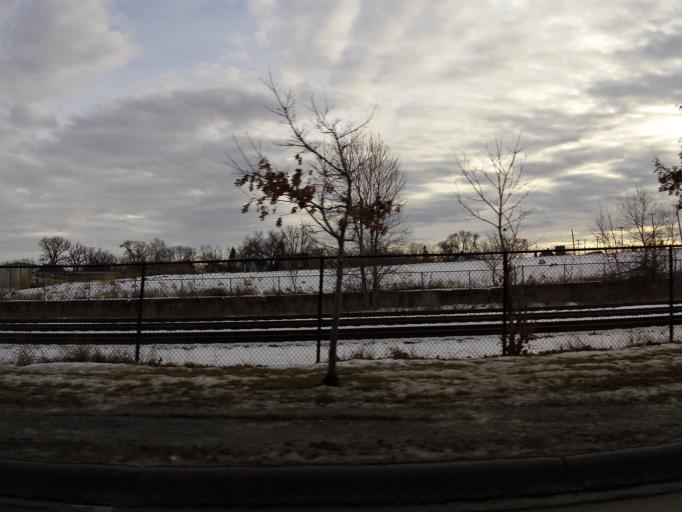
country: US
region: Minnesota
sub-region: Ramsey County
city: Saint Paul
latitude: 44.9661
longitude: -93.0602
